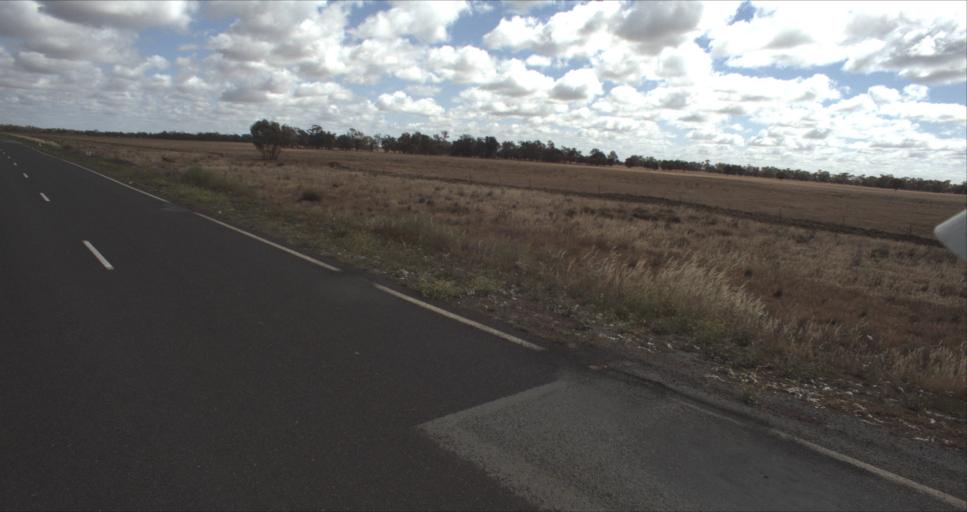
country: AU
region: New South Wales
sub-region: Murrumbidgee Shire
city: Darlington Point
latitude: -34.5791
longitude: 146.1086
